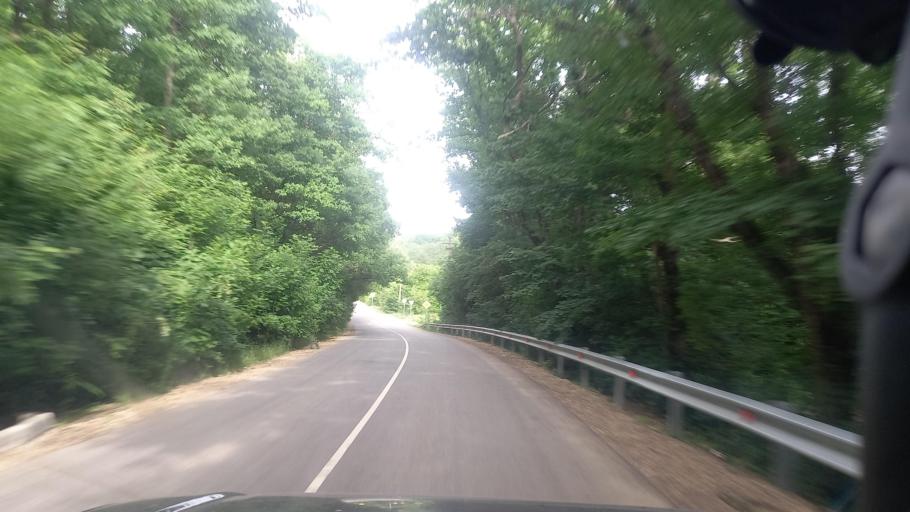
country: RU
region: Krasnodarskiy
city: Goryachiy Klyuch
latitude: 44.6038
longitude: 39.0044
